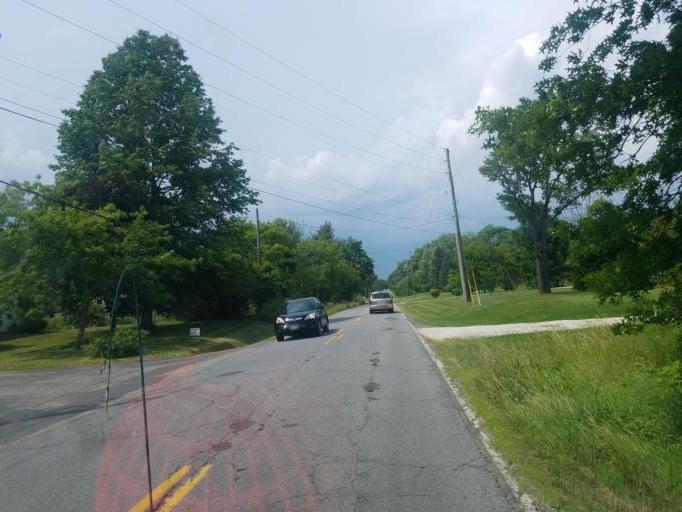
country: US
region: Ohio
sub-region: Portage County
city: Ravenna
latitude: 41.1105
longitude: -81.2202
